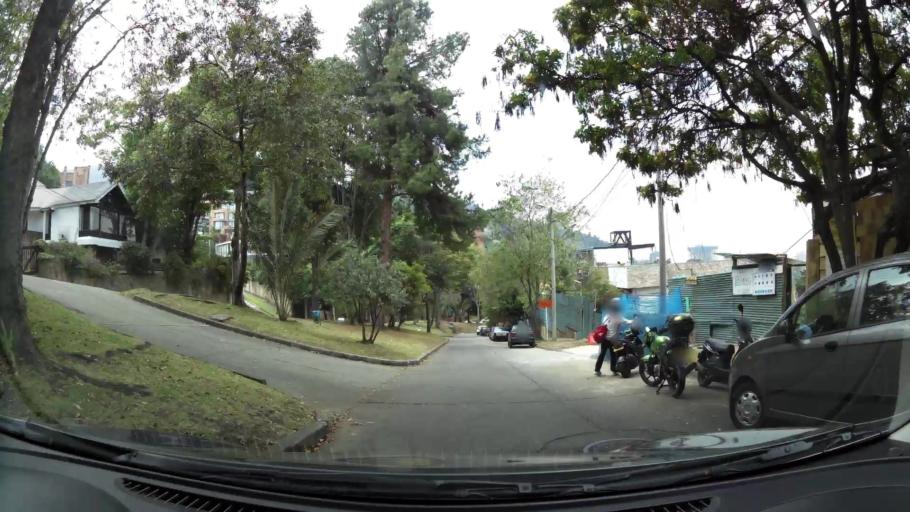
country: CO
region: Bogota D.C.
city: Barrio San Luis
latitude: 4.6859
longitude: -74.0278
